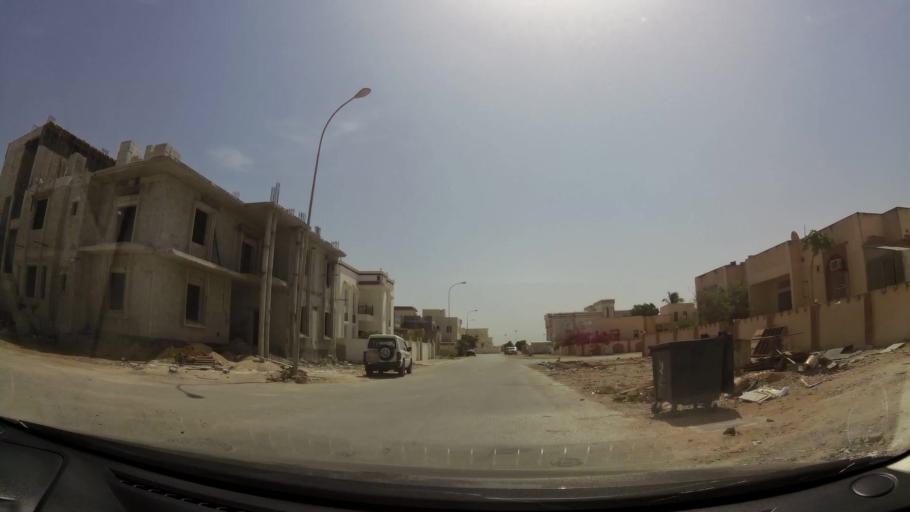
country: OM
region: Zufar
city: Salalah
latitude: 17.0405
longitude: 54.1507
